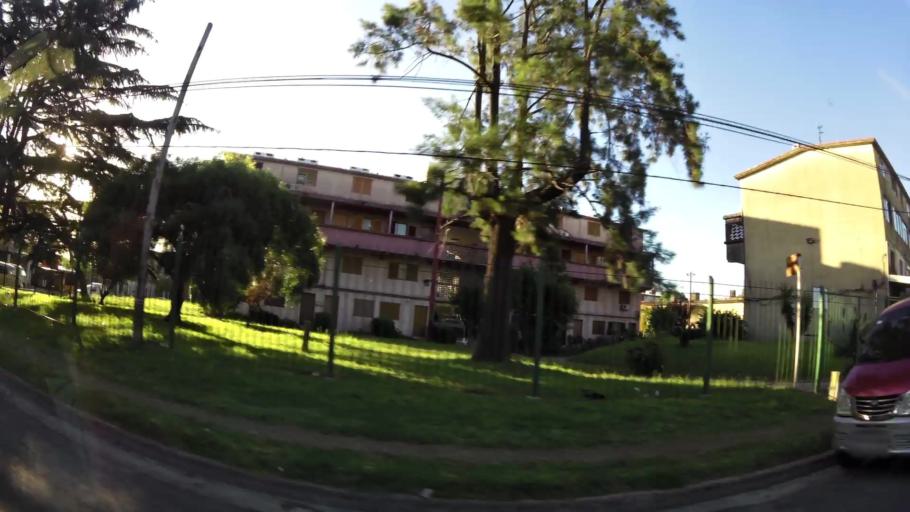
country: UY
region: Montevideo
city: Montevideo
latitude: -34.8427
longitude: -56.2120
